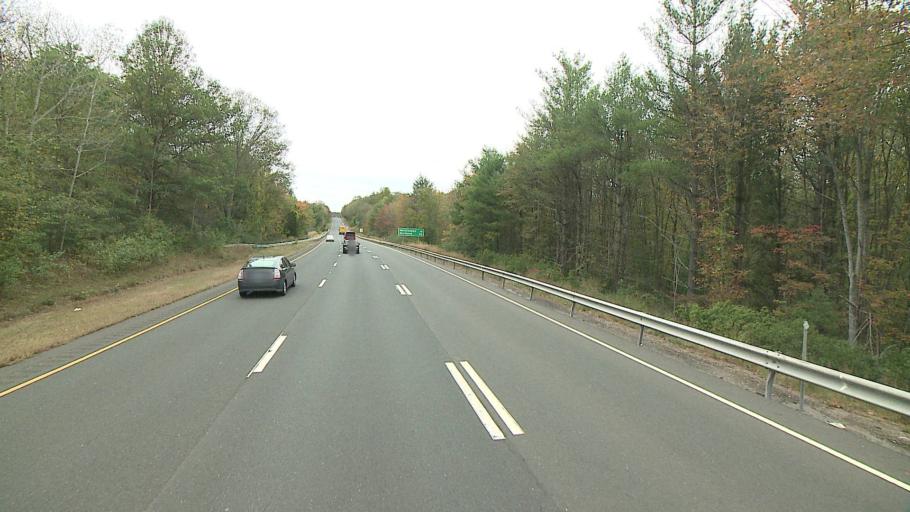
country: US
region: Connecticut
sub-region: Middlesex County
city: Higganum
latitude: 41.4632
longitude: -72.5372
